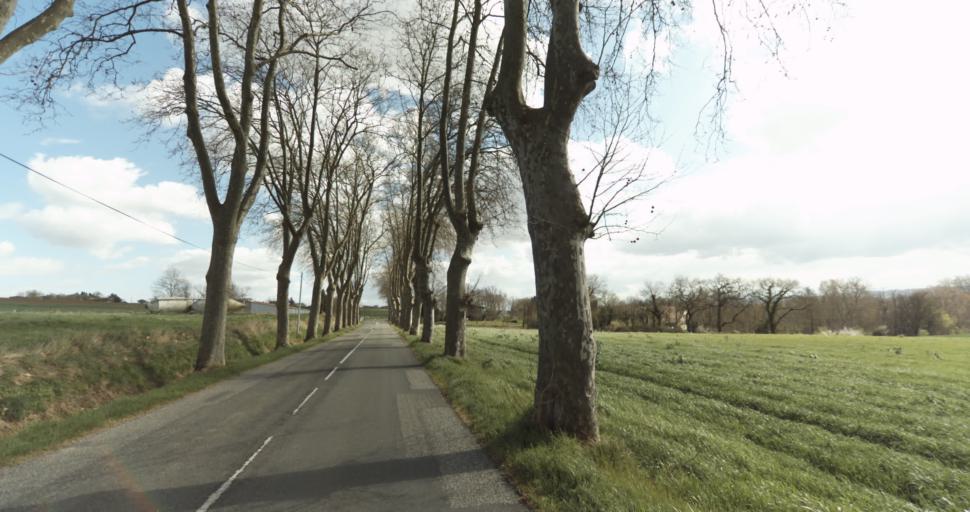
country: FR
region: Midi-Pyrenees
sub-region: Departement de la Haute-Garonne
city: Auterive
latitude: 43.3671
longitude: 1.4738
